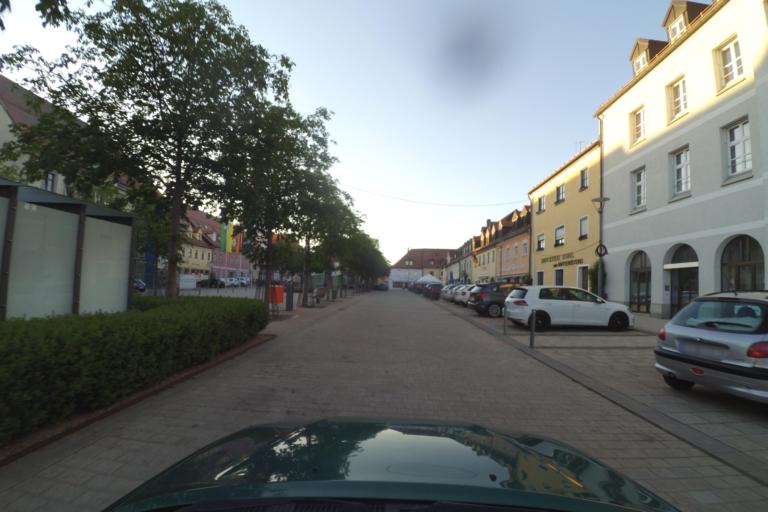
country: DE
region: Bavaria
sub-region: Upper Palatinate
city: Tirschenreuth
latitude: 49.8783
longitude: 12.3374
